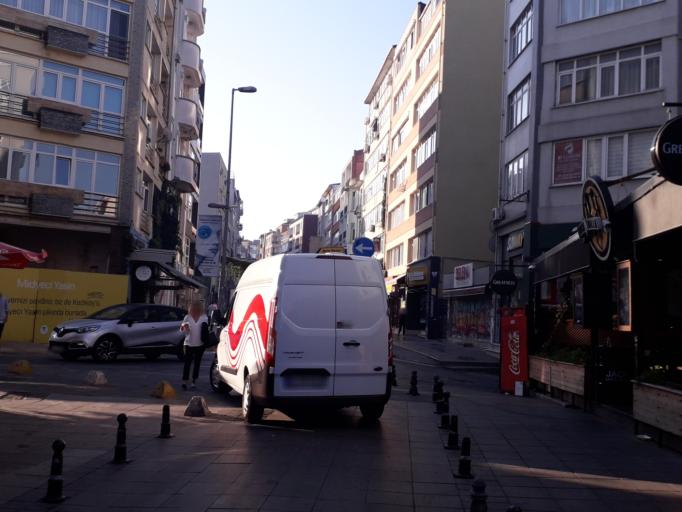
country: TR
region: Istanbul
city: UEskuedar
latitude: 40.9890
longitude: 29.0248
